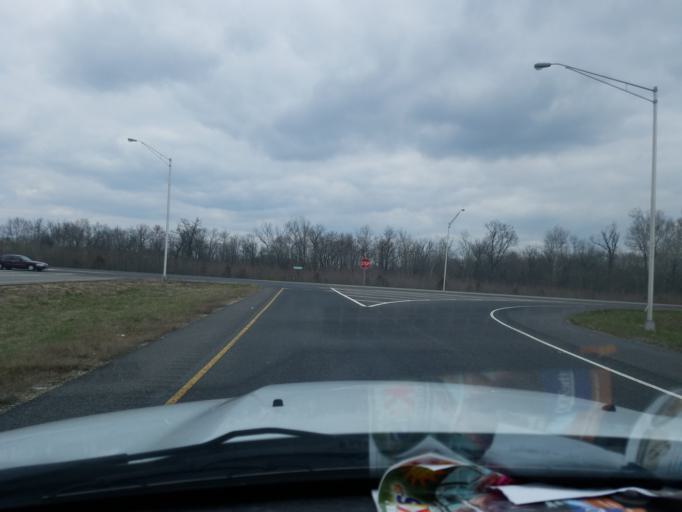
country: US
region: Indiana
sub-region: Vigo County
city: Terre Haute
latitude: 39.3974
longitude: -87.3699
